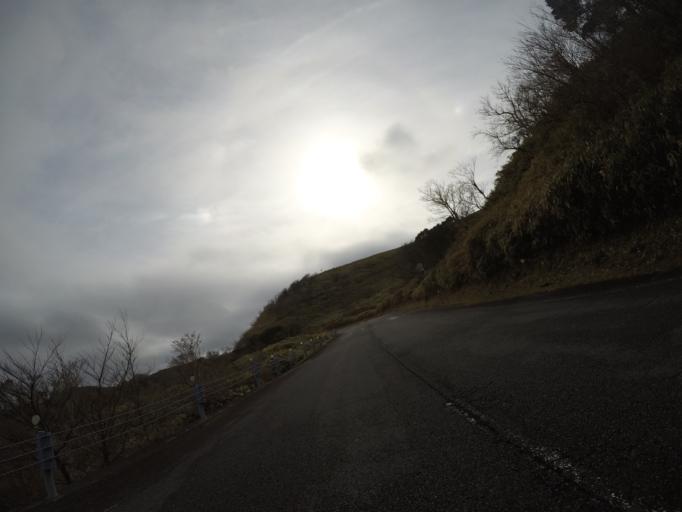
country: JP
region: Shizuoka
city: Heda
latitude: 34.8664
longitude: 138.8410
